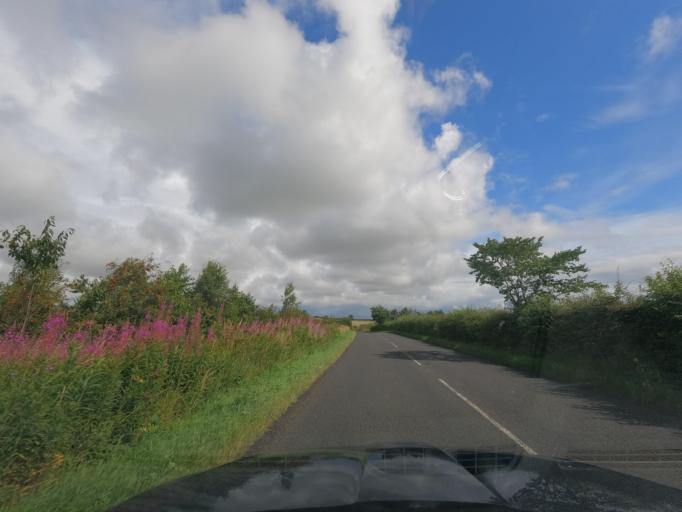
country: GB
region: England
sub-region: Northumberland
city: Lowick
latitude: 55.6187
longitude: -1.9927
